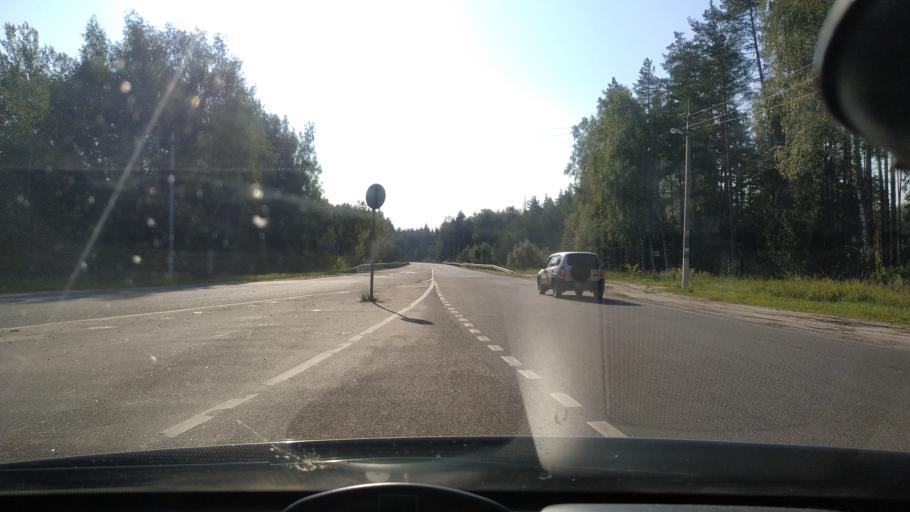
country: RU
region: Moskovskaya
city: Kerva
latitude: 55.5660
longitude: 39.6509
